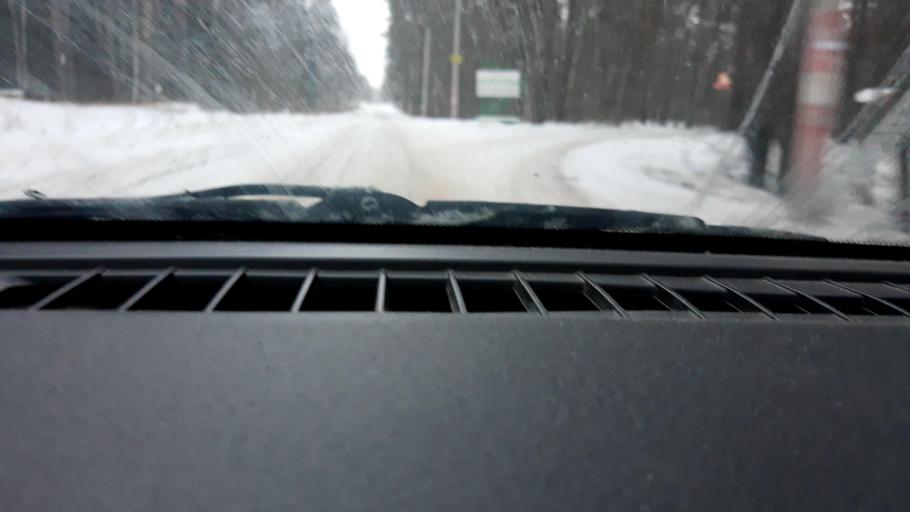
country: RU
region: Nizjnij Novgorod
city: Afonino
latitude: 56.1734
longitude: 44.0850
